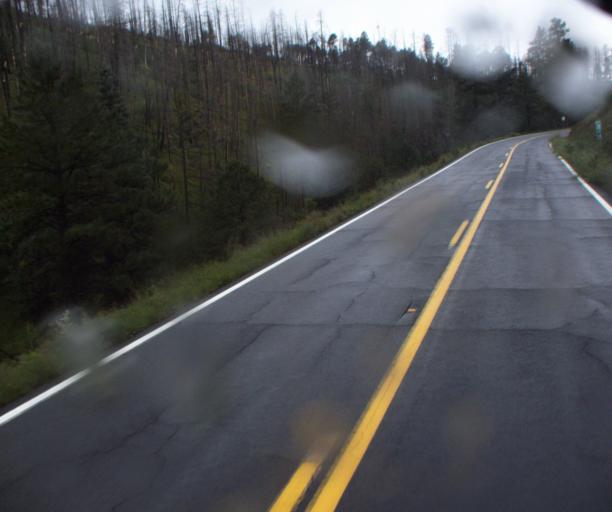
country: US
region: Arizona
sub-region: Apache County
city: Eagar
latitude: 33.7477
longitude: -109.2098
